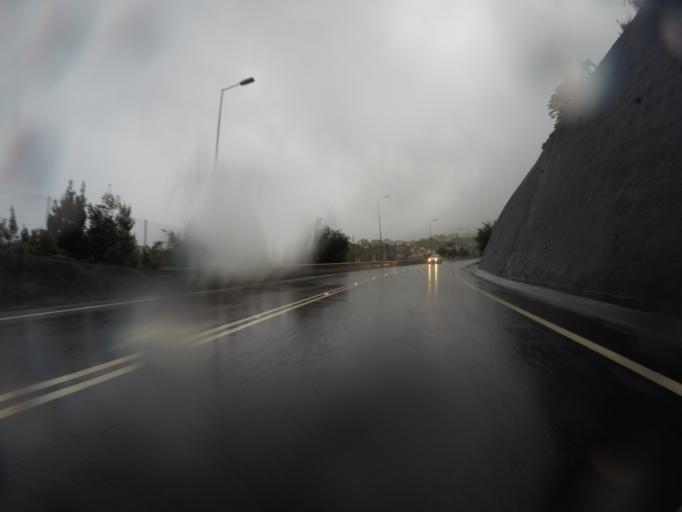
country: PT
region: Madeira
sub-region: Santana
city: Santana
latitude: 32.7630
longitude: -16.8312
